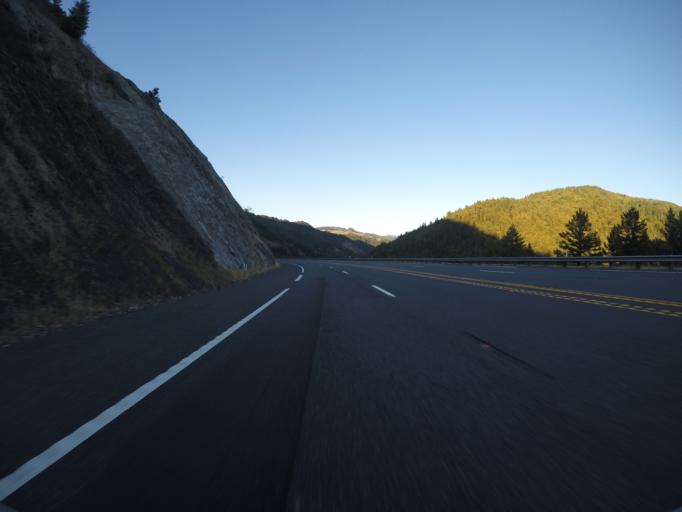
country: US
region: California
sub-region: Mendocino County
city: Laytonville
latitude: 39.8288
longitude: -123.6544
